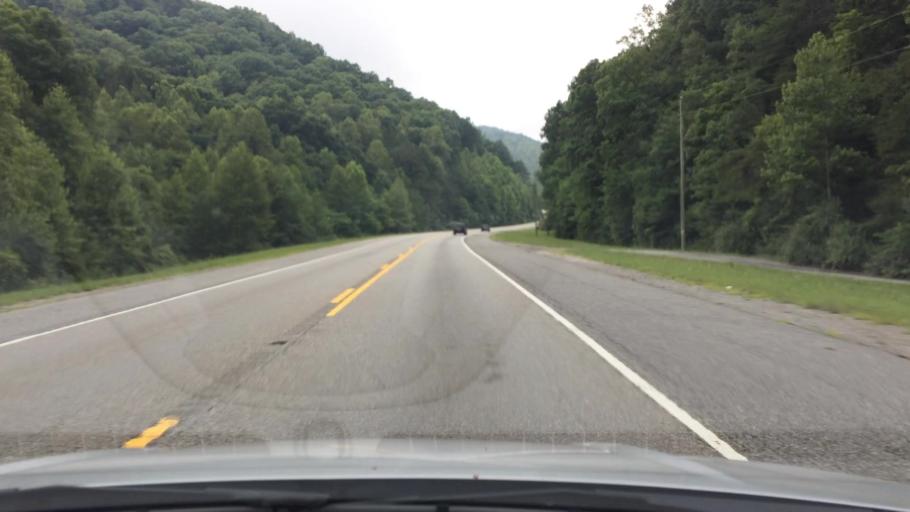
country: US
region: Tennessee
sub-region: Campbell County
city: Caryville
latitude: 36.4062
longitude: -84.3070
